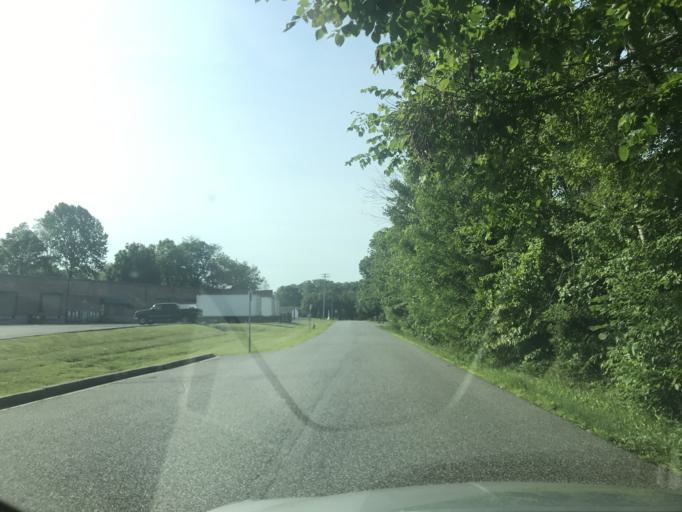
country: US
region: Maryland
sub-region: Harford County
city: Bel Air North
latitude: 39.5678
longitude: -76.3655
